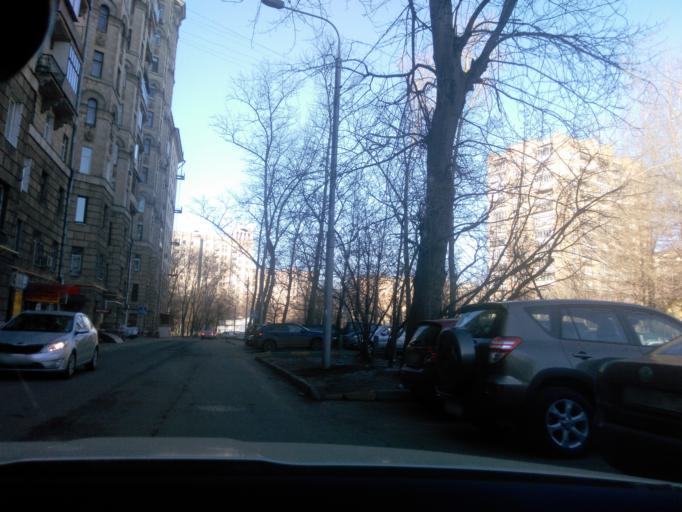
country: RU
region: Moskovskaya
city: Koptevo
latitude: 55.8167
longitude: 37.5084
